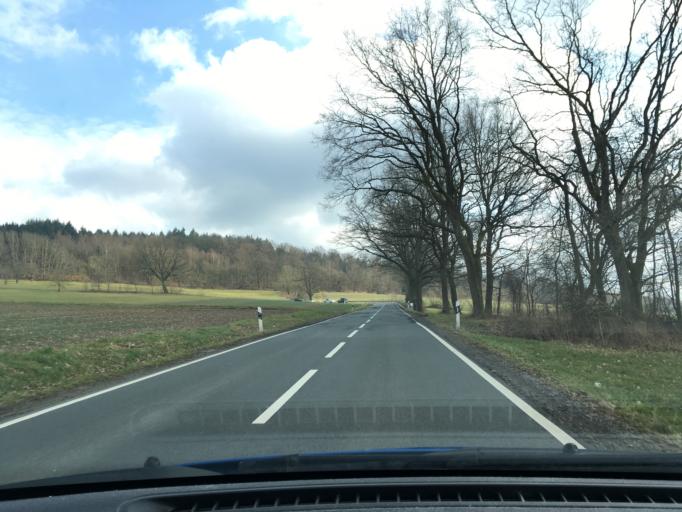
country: DE
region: Lower Saxony
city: Uslar
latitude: 51.5898
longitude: 9.6085
